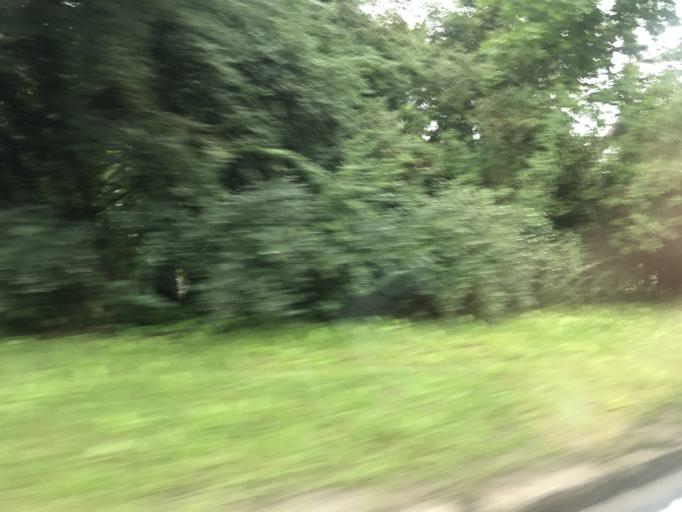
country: PL
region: Warmian-Masurian Voivodeship
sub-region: Powiat elblaski
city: Elblag
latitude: 54.1632
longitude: 19.4170
